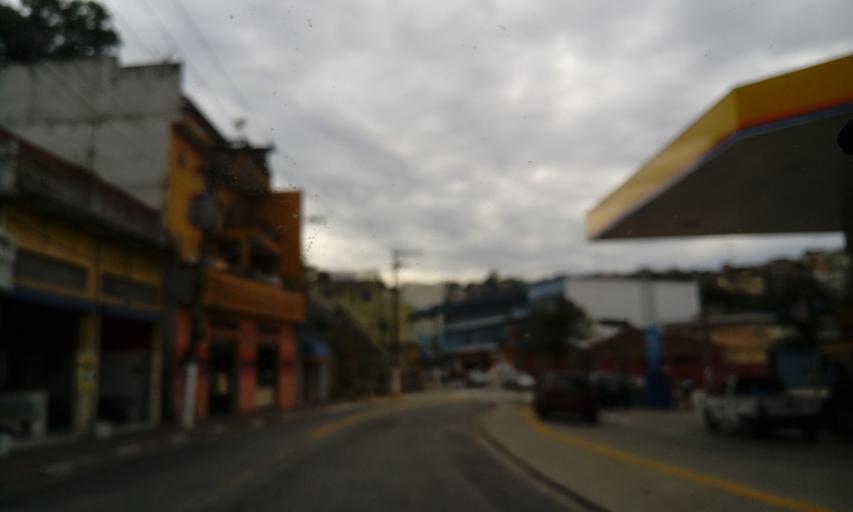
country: BR
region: Sao Paulo
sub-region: Caieiras
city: Caieiras
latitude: -23.4044
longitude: -46.7508
